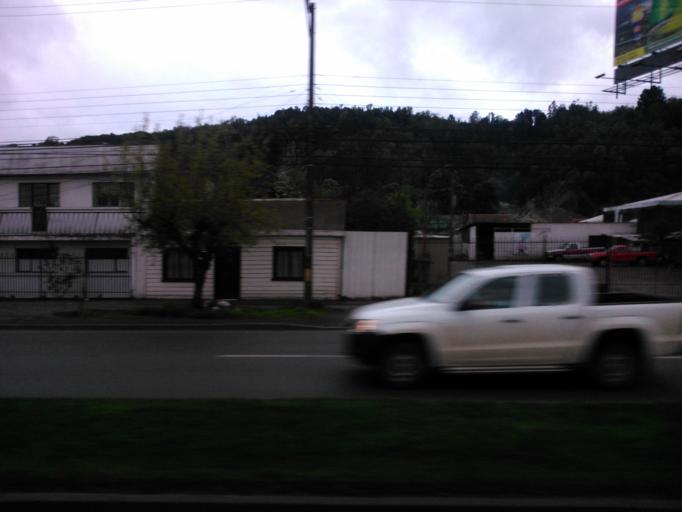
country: CL
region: Araucania
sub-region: Provincia de Cautin
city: Temuco
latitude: -38.7295
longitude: -72.5817
